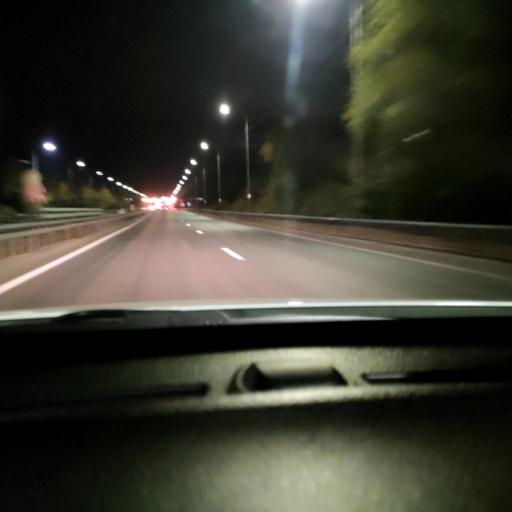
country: RU
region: Voronezj
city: Pridonskoy
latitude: 51.6495
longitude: 39.0845
